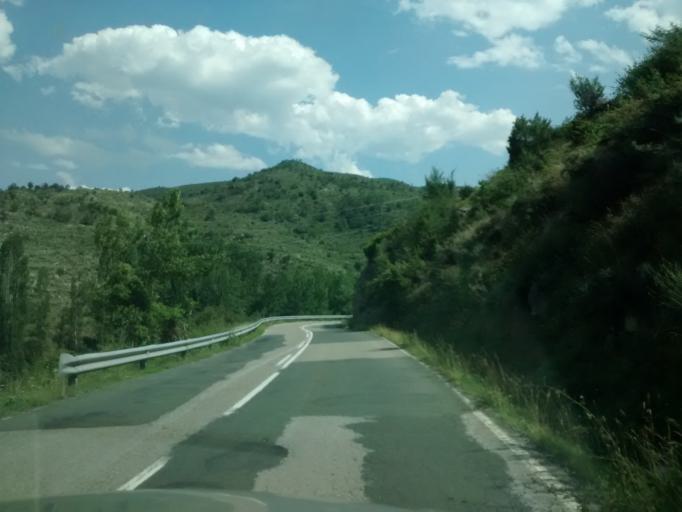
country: ES
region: La Rioja
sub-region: Provincia de La Rioja
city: Terroba
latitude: 42.2505
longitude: -2.4544
